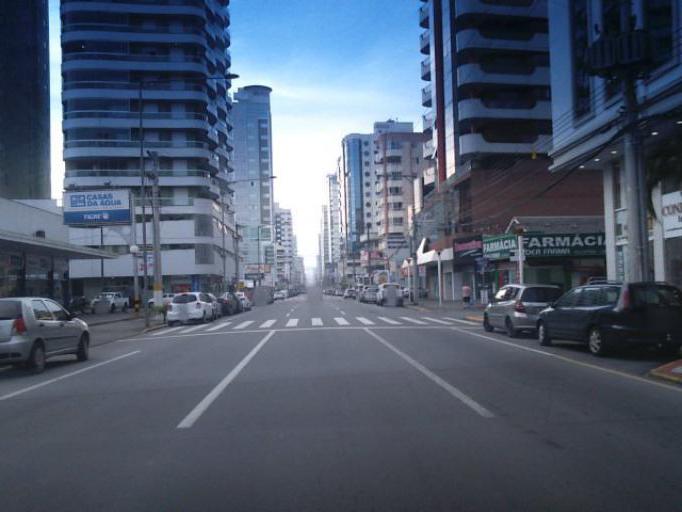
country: BR
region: Santa Catarina
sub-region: Itapema
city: Itapema
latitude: -27.1207
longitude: -48.6070
